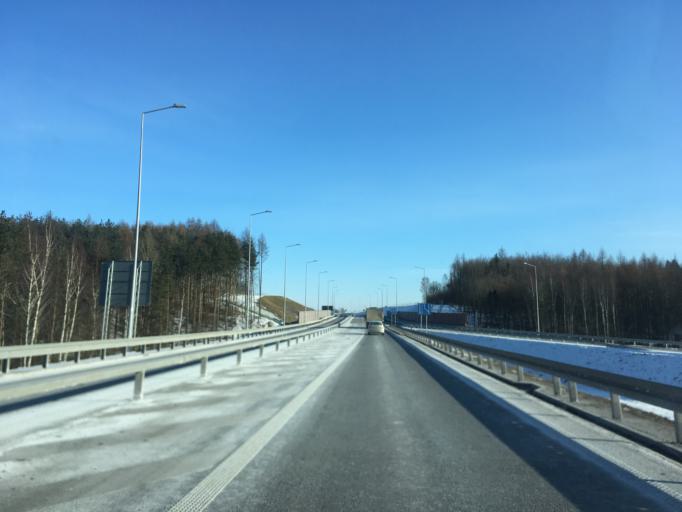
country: PL
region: Pomeranian Voivodeship
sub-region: Powiat koscierski
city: Koscierzyna
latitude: 54.1107
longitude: 17.9552
